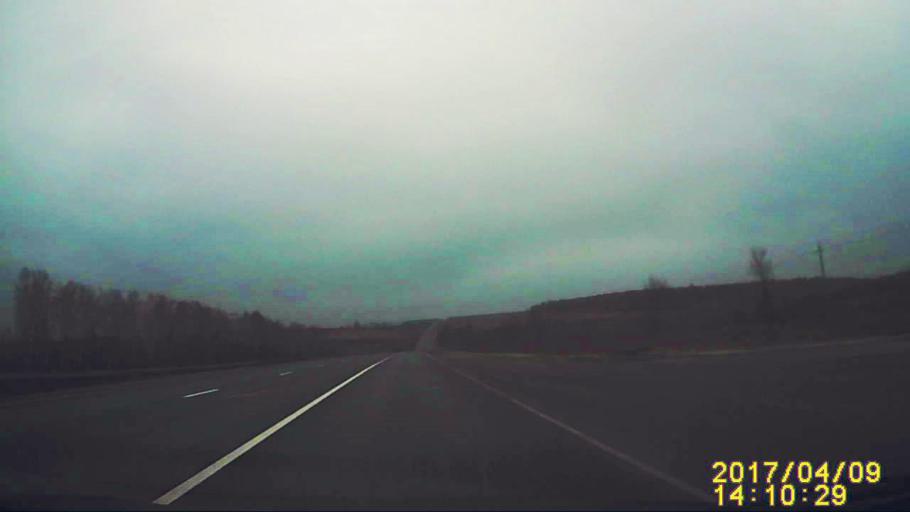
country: RU
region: Ulyanovsk
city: Krasnyy Gulyay
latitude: 54.0388
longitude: 48.2135
